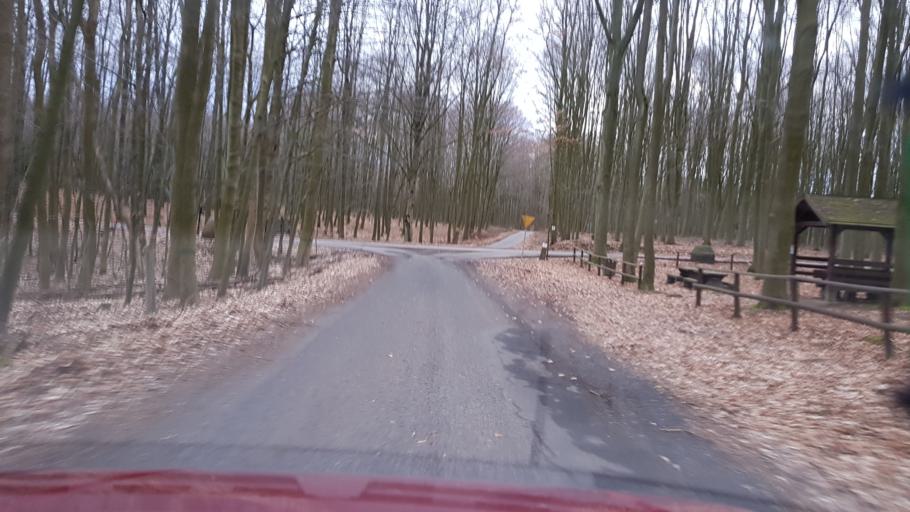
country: PL
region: West Pomeranian Voivodeship
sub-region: Powiat gryfinski
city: Stare Czarnowo
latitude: 53.3183
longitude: 14.7133
